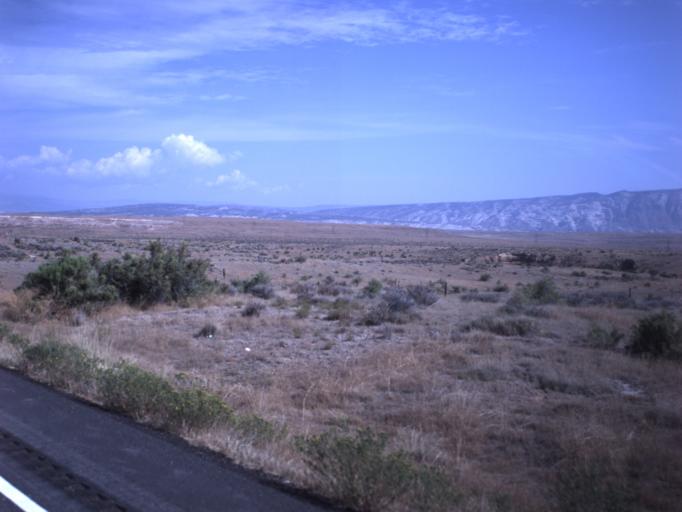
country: US
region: Utah
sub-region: Uintah County
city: Naples
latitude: 40.3516
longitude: -109.3082
